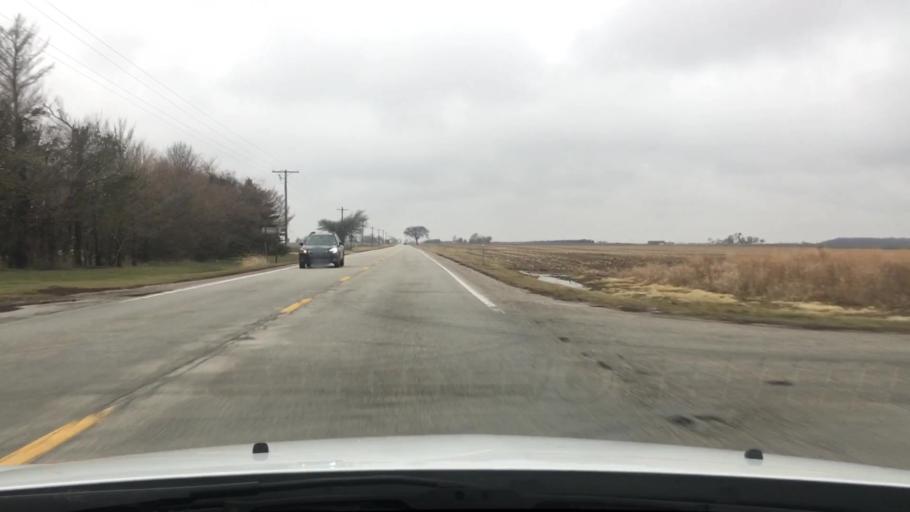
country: US
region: Illinois
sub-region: Iroquois County
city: Clifton
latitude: 40.8876
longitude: -87.8467
